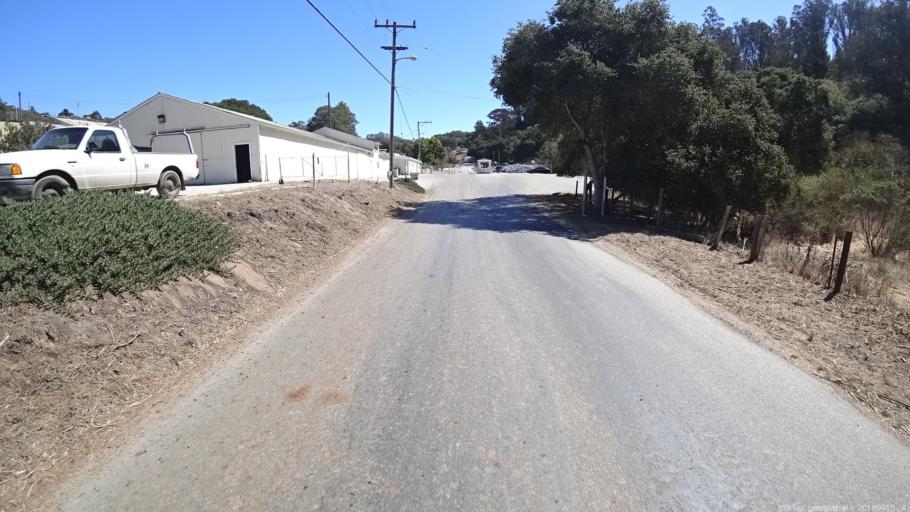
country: US
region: California
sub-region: San Benito County
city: Aromas
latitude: 36.8344
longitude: -121.6627
